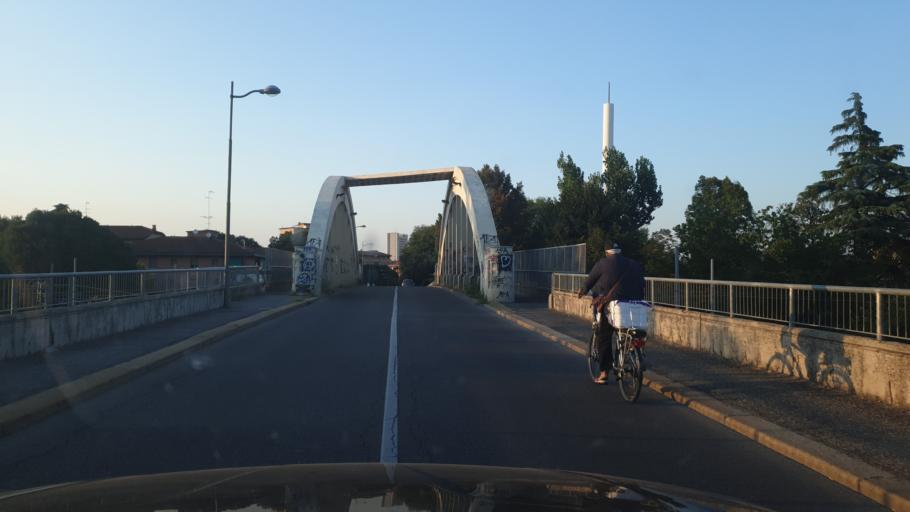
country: IT
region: Emilia-Romagna
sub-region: Provincia di Bologna
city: Bologna
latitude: 44.4988
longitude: 11.3656
